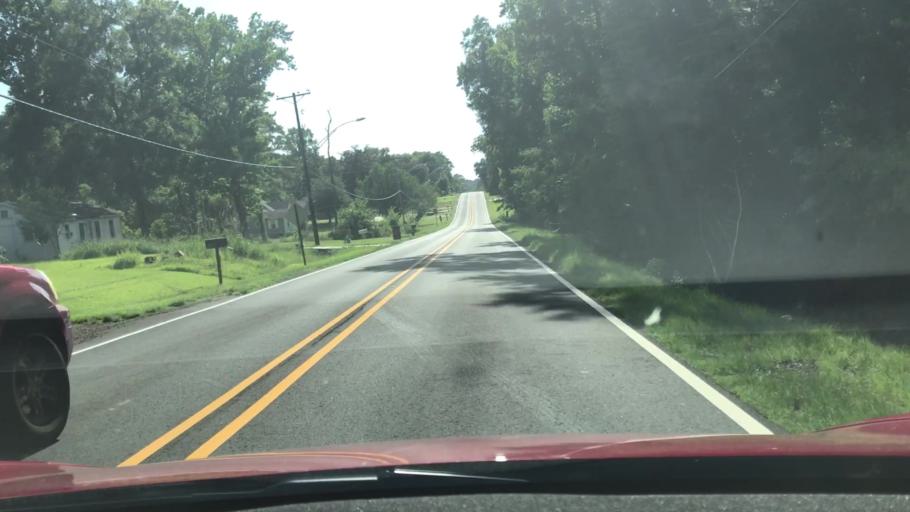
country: US
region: Louisiana
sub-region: Bossier Parish
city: Bossier City
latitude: 32.3910
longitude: -93.7564
